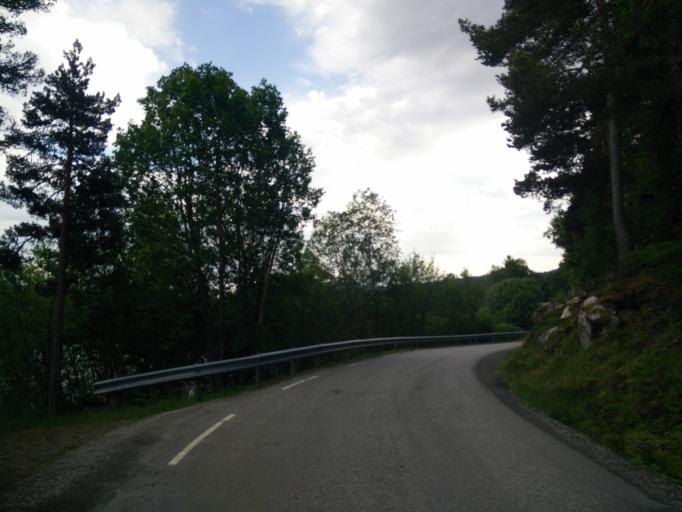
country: NO
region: More og Romsdal
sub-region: Kristiansund
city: Rensvik
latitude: 63.0262
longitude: 7.9530
